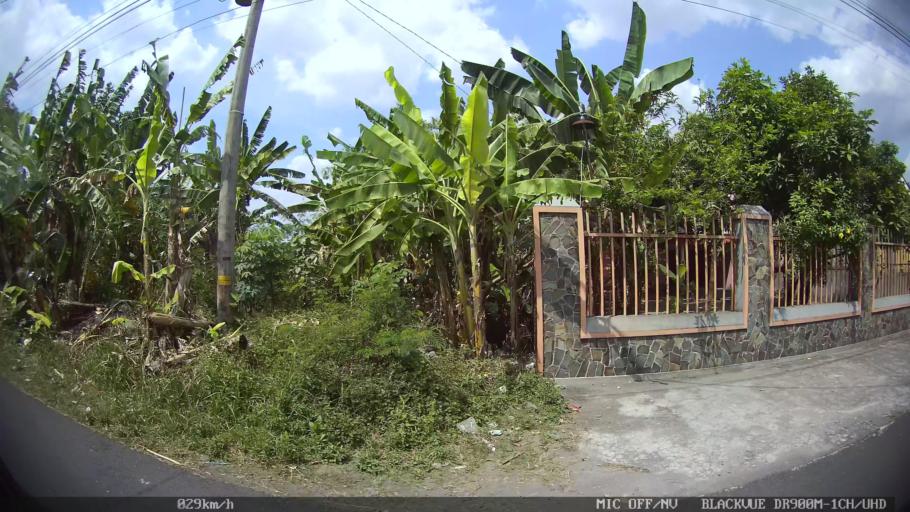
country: ID
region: Daerah Istimewa Yogyakarta
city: Kasihan
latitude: -7.8119
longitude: 110.3402
